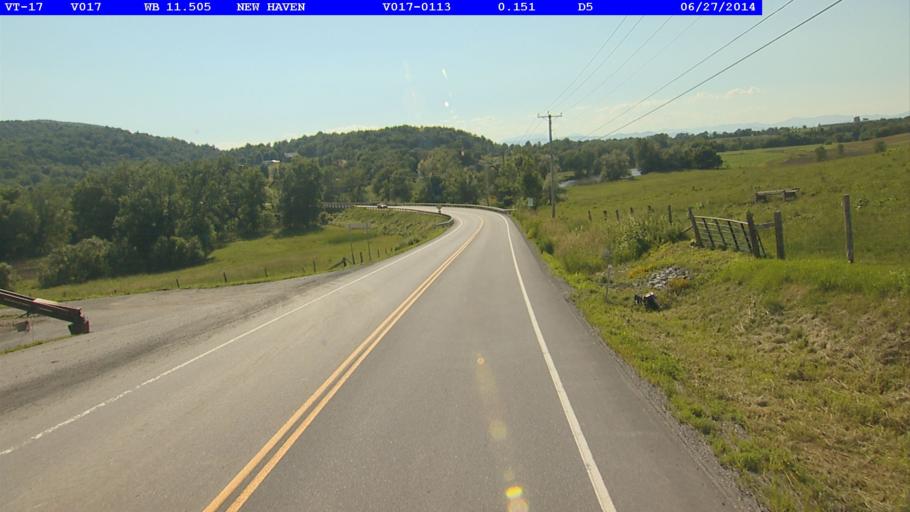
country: US
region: Vermont
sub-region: Addison County
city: Vergennes
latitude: 44.0864
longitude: -73.2436
